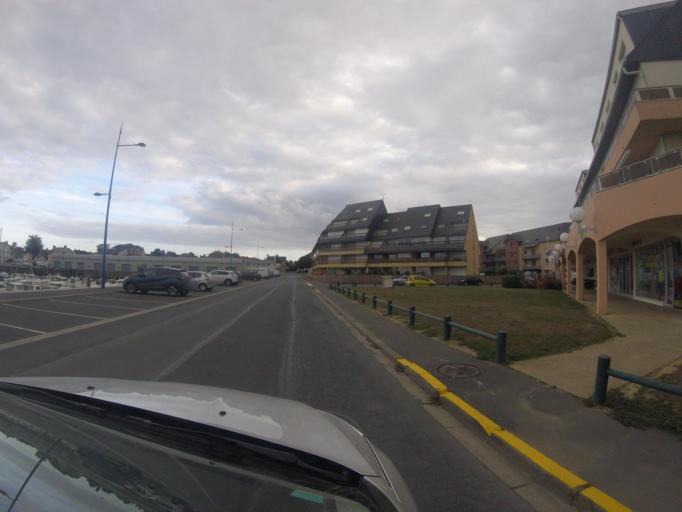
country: FR
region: Lower Normandy
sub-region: Departement du Calvados
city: Grandcamp-Maisy
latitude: 49.3885
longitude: -1.0506
